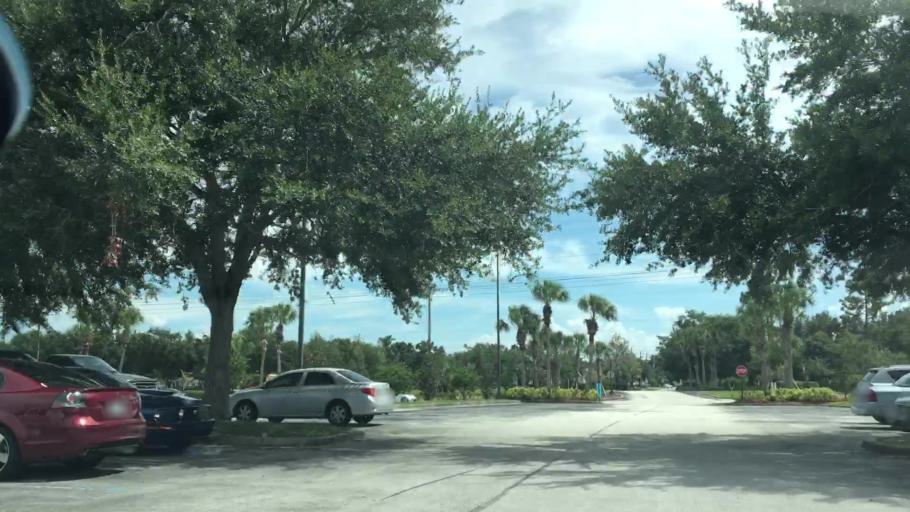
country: US
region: Florida
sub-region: Volusia County
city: Deltona
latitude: 28.9134
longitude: -81.2895
